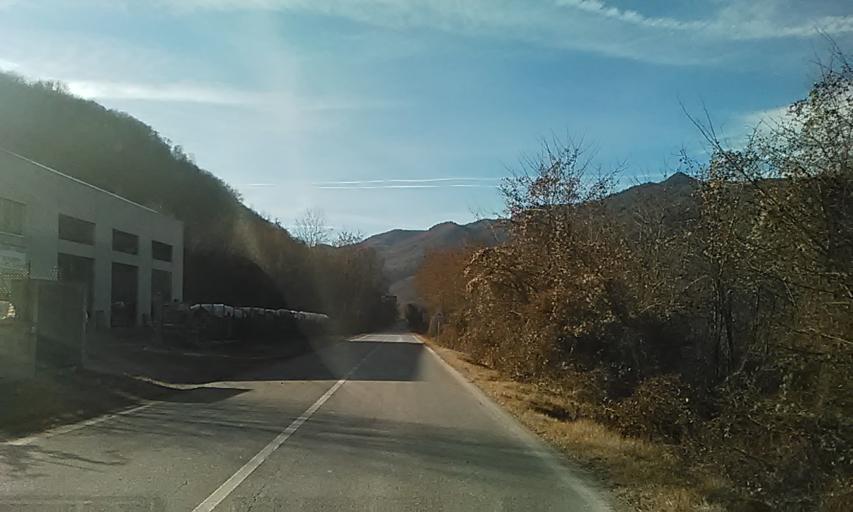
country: IT
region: Piedmont
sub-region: Provincia di Vercelli
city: Quarona
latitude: 45.7787
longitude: 8.2742
